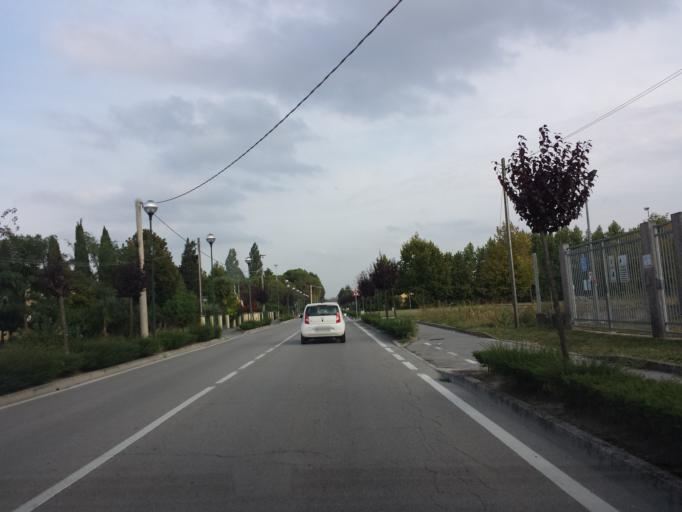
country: IT
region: Veneto
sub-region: Provincia di Padova
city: Campodarsego
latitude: 45.4991
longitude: 11.9220
